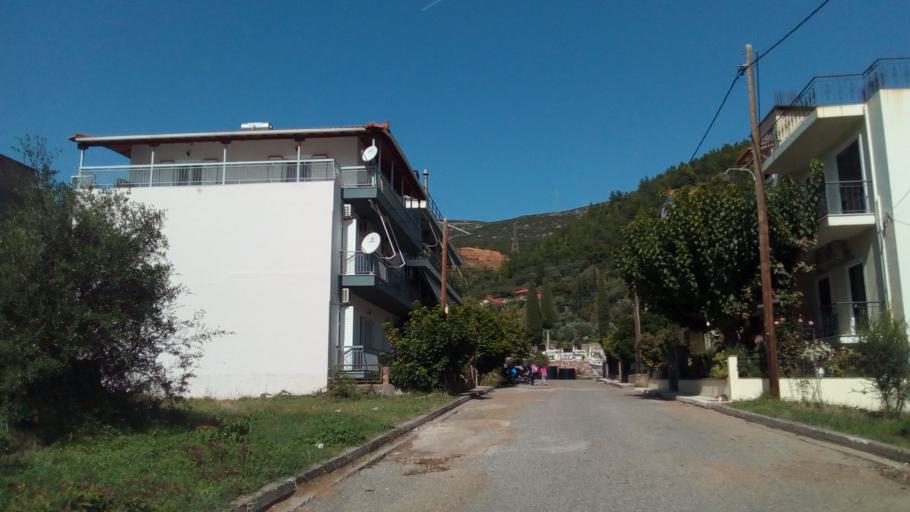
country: GR
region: West Greece
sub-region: Nomos Aitolias kai Akarnanias
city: Nafpaktos
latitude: 38.3927
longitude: 21.8195
